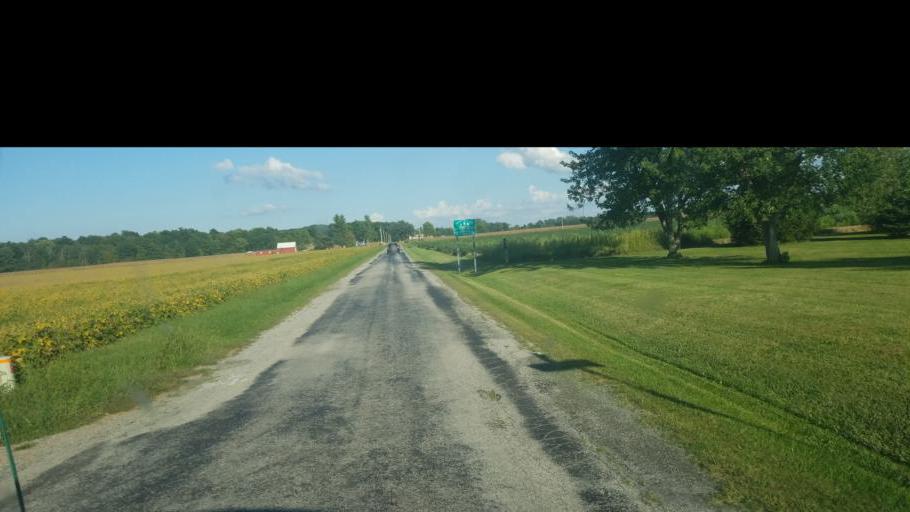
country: US
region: Ohio
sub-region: Hancock County
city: Arlington
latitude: 40.9352
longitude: -83.5655
